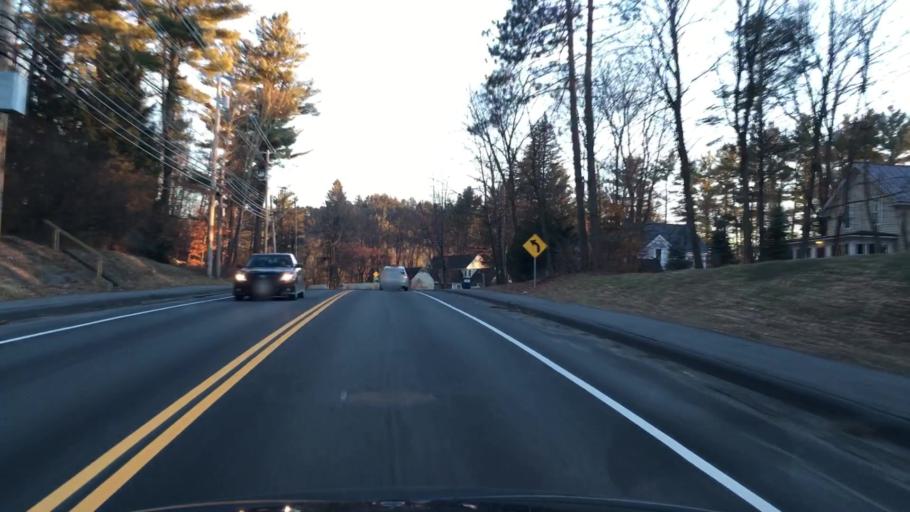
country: US
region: New Hampshire
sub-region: Grafton County
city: Hanover
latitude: 43.6946
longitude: -72.2792
